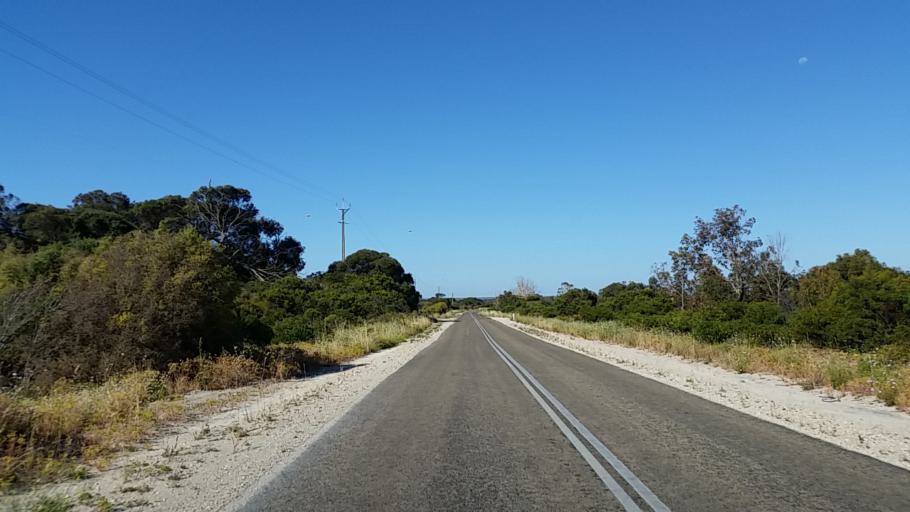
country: AU
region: South Australia
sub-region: Yorke Peninsula
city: Honiton
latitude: -35.2278
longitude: 136.9862
